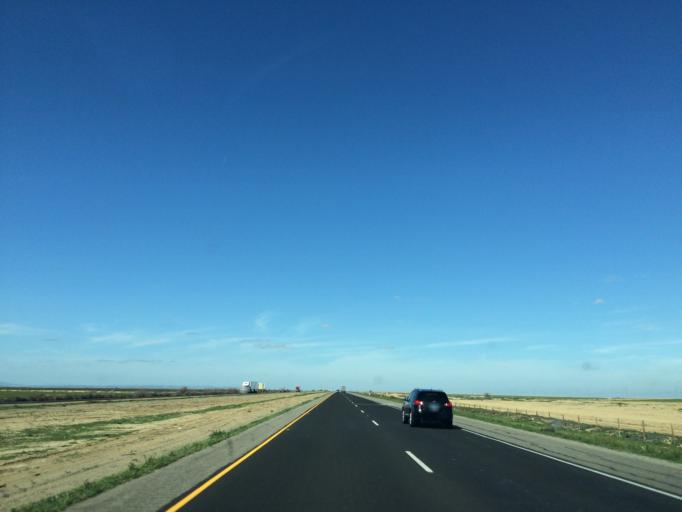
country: US
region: California
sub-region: Kern County
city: Lost Hills
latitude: 35.7436
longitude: -119.7479
